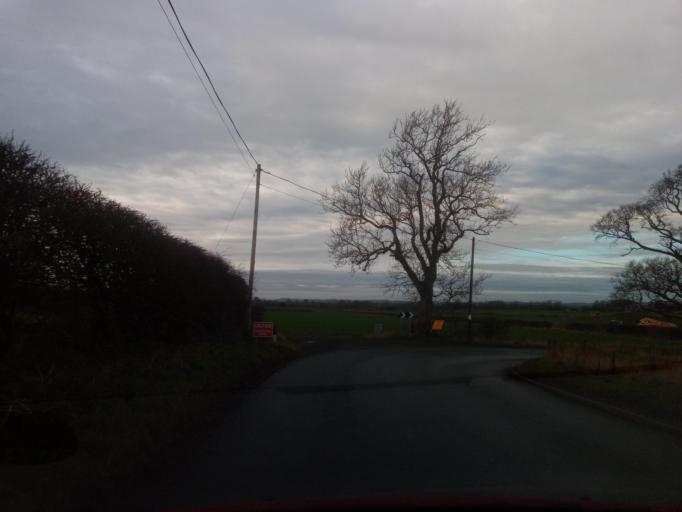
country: GB
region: Scotland
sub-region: The Scottish Borders
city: Coldstream
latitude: 55.7181
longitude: -2.2542
